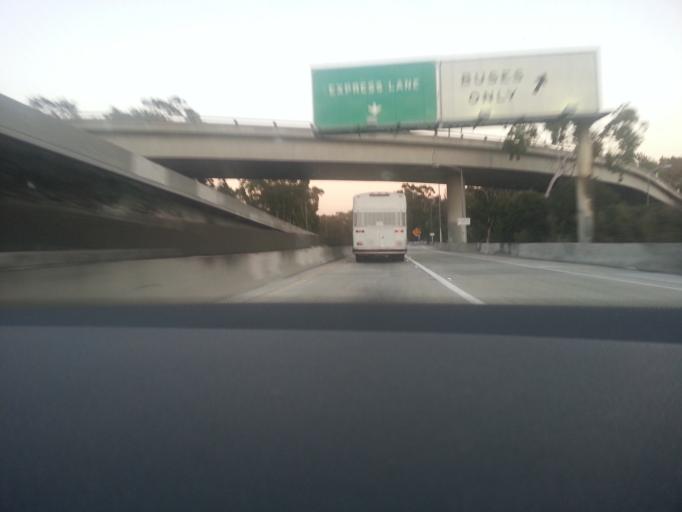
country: US
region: California
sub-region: Los Angeles County
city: Belvedere
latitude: 34.0625
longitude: -118.1659
